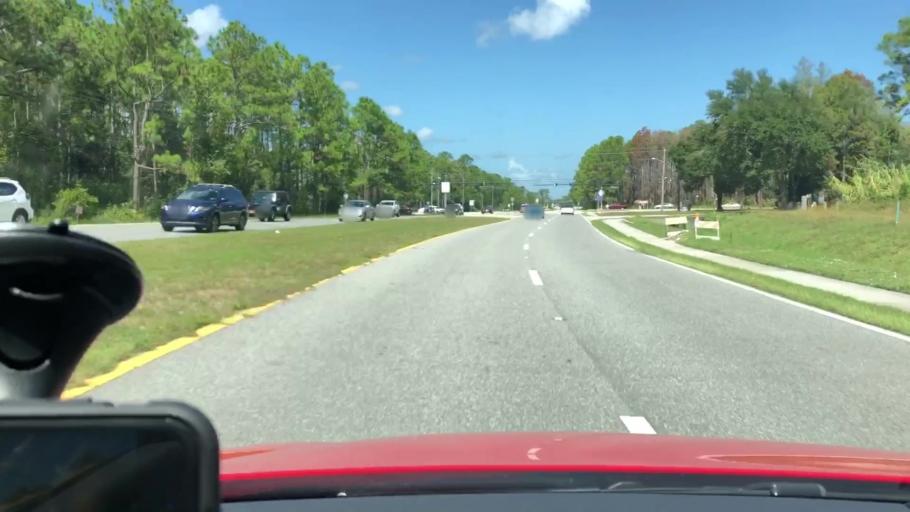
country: US
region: Florida
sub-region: Volusia County
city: Holly Hill
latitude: 29.2078
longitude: -81.0742
